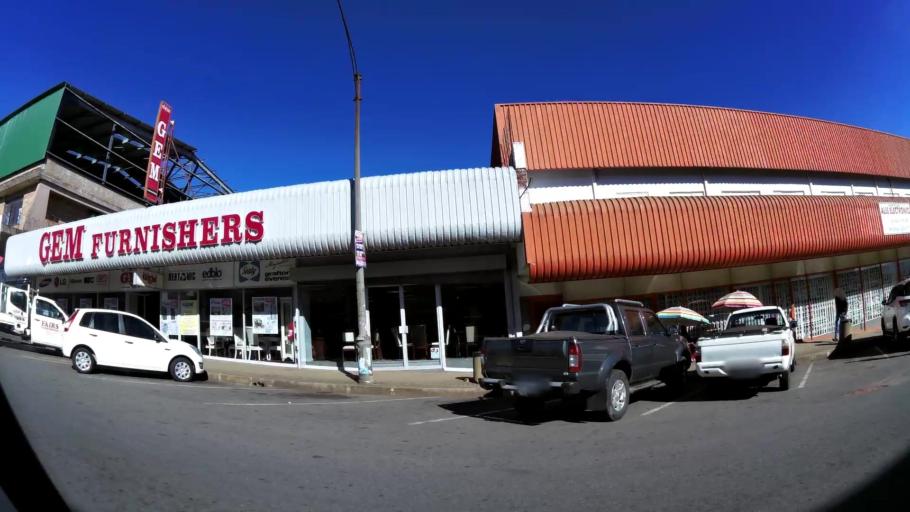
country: ZA
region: Limpopo
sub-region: Mopani District Municipality
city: Tzaneen
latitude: -23.8264
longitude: 30.1605
